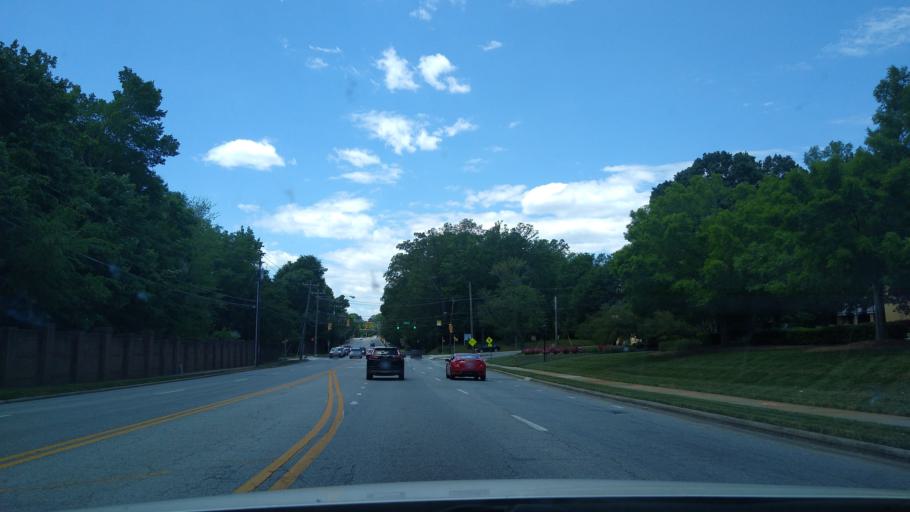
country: US
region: North Carolina
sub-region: Guilford County
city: Greensboro
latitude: 36.0861
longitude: -79.8397
